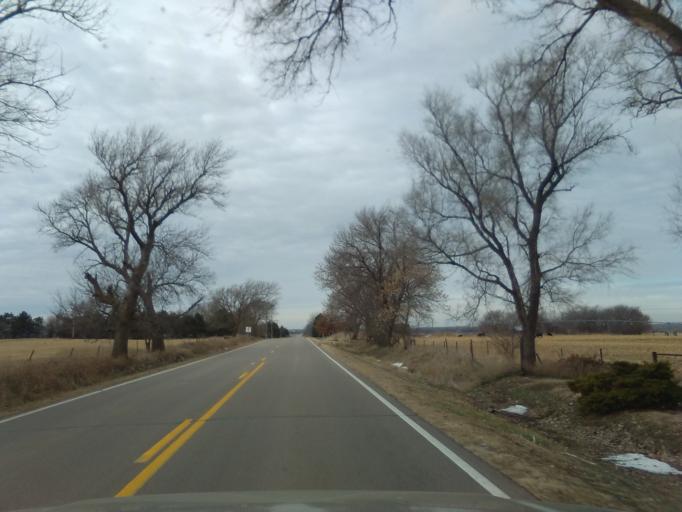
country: US
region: Nebraska
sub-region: Hall County
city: Grand Island
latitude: 40.7710
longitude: -98.3855
